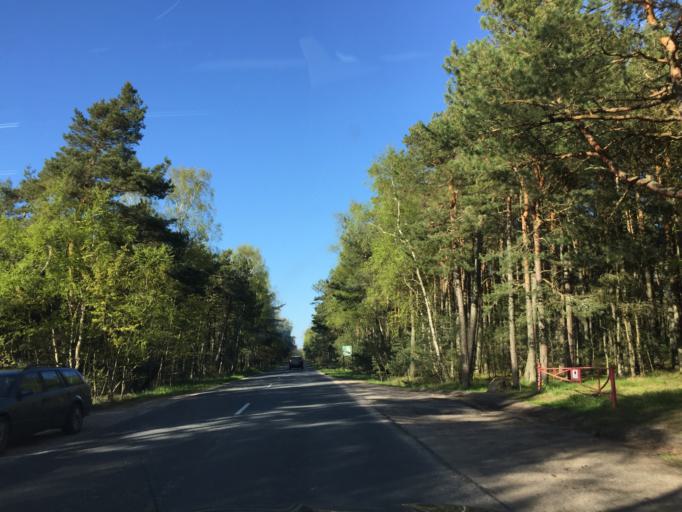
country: LT
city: Nida
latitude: 55.2067
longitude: 20.8754
